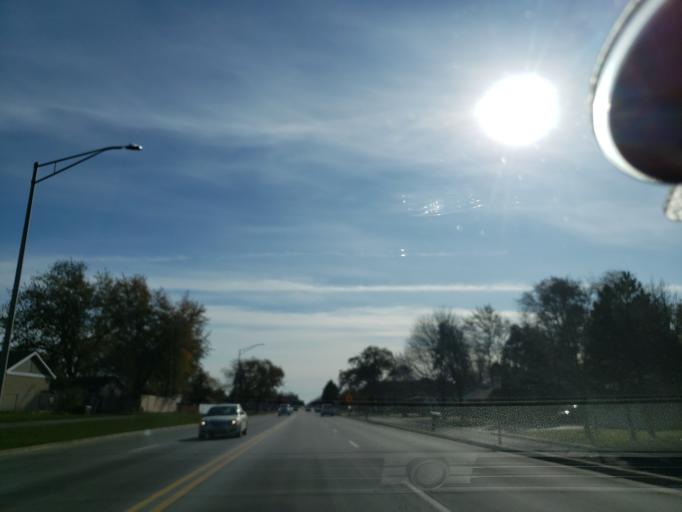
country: US
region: Illinois
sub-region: Cook County
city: Tinley Park
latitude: 41.5919
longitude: -87.7849
